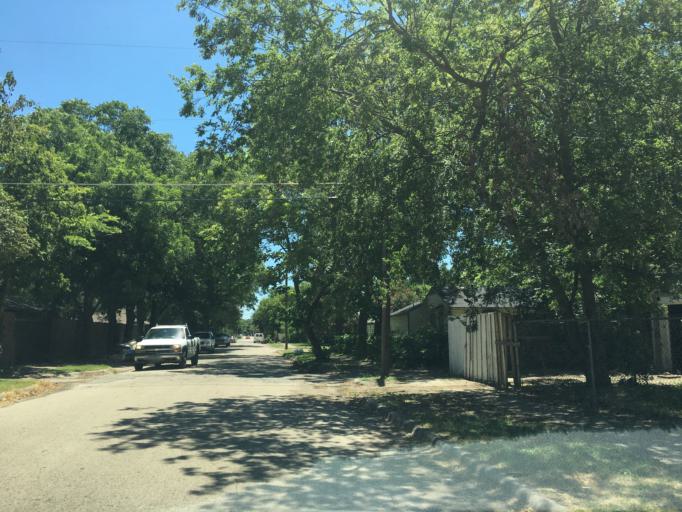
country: US
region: Texas
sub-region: Dallas County
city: Garland
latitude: 32.8474
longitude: -96.6802
